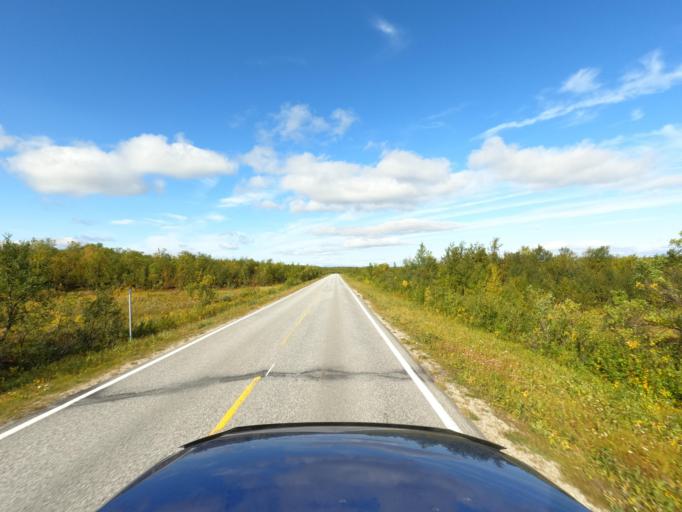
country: NO
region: Finnmark Fylke
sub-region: Karasjok
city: Karasjohka
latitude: 69.5904
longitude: 25.3389
